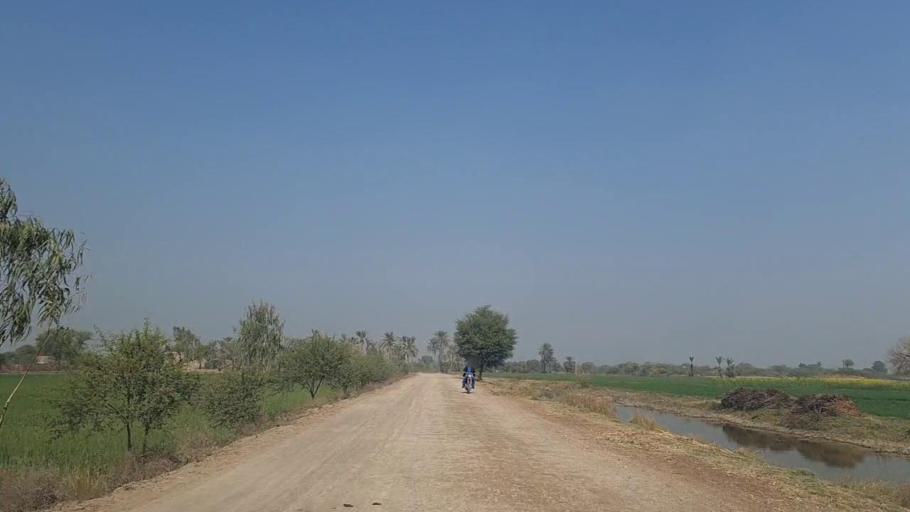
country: PK
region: Sindh
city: Nawabshah
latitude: 26.2332
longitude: 68.4940
